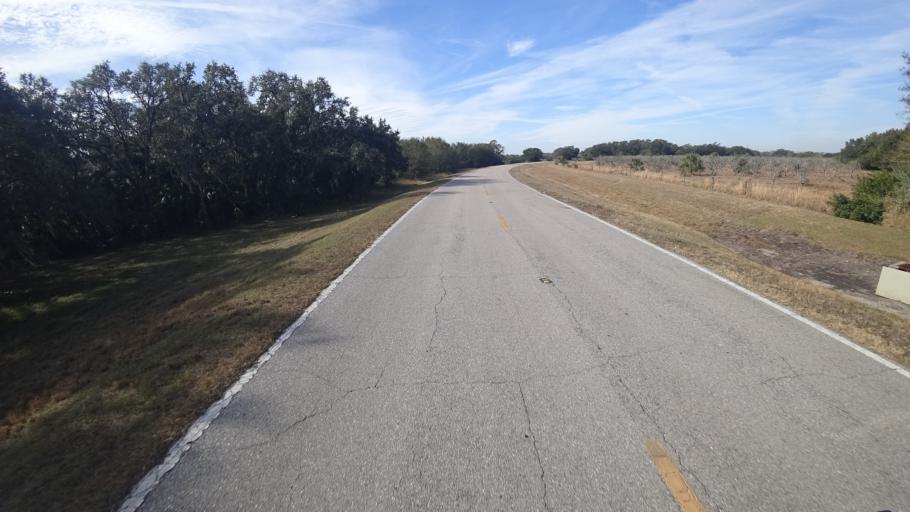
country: US
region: Florida
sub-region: Hillsborough County
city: Ruskin
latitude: 27.6241
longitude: -82.4524
